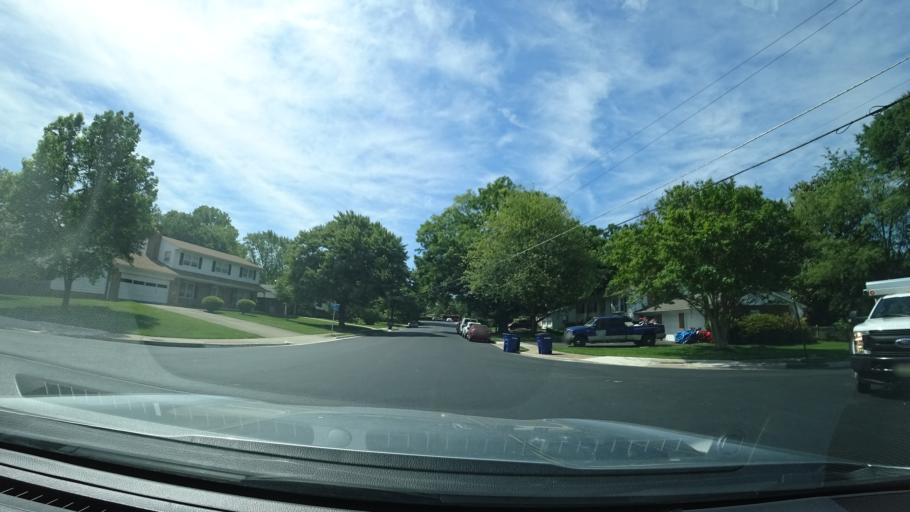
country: US
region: Virginia
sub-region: Fairfax County
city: Herndon
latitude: 38.9706
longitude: -77.3946
